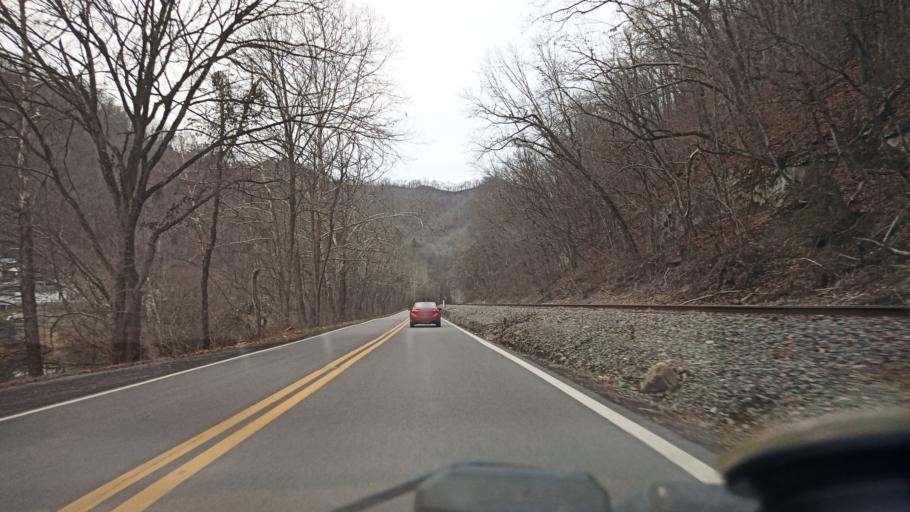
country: US
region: West Virginia
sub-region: Logan County
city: Mallory
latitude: 37.7221
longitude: -81.8714
